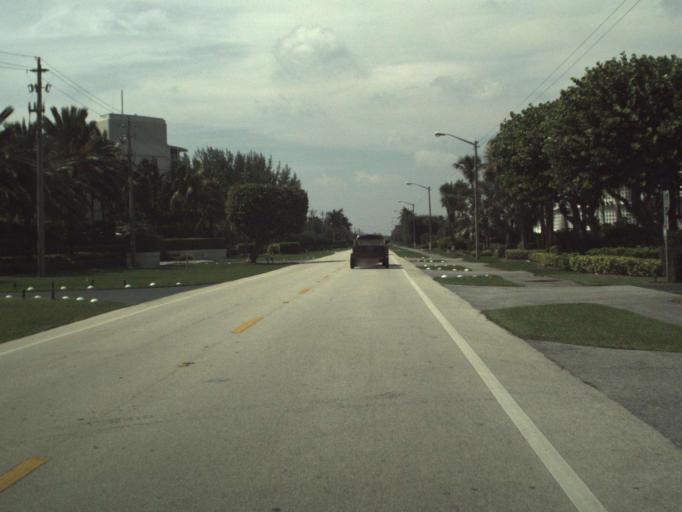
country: US
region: Florida
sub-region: Palm Beach County
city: Lake Worth
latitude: 26.6229
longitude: -80.0388
